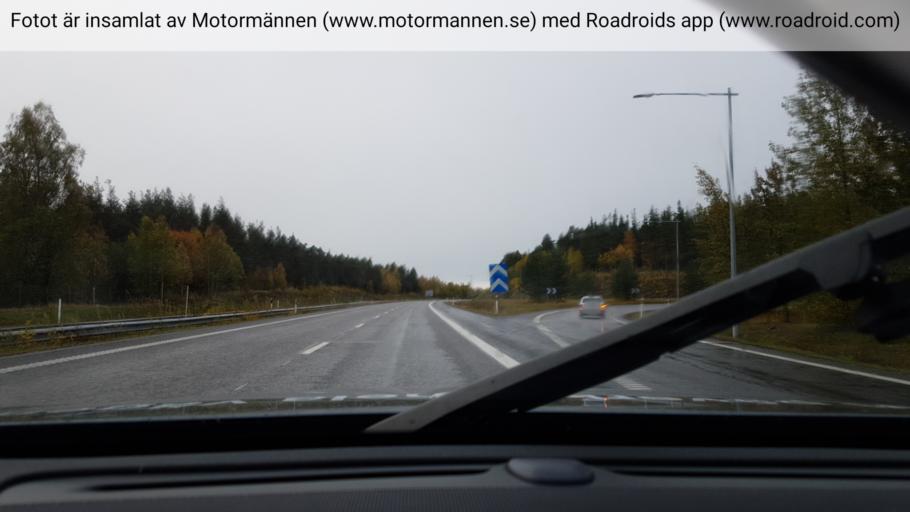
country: SE
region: Norrbotten
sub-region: Pitea Kommun
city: Pitea
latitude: 65.3319
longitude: 21.4409
